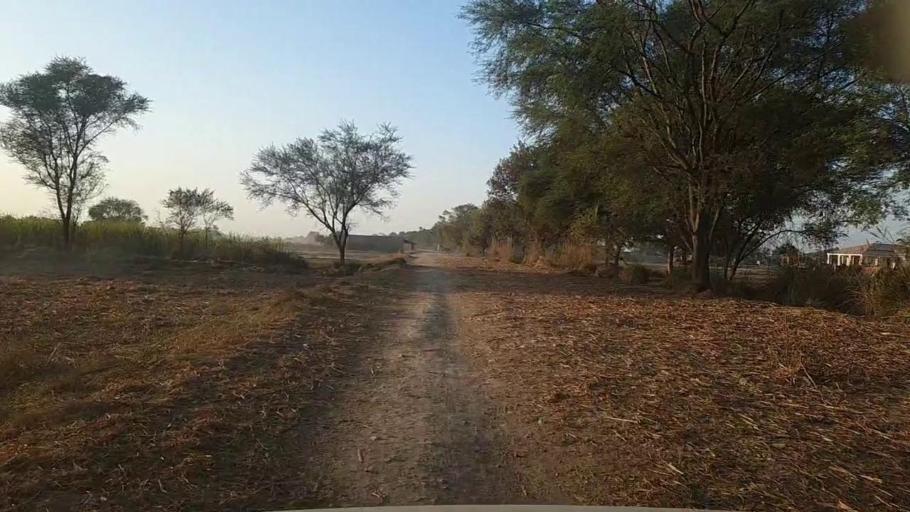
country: PK
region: Sindh
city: Mirpur Mathelo
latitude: 27.8937
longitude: 69.6562
